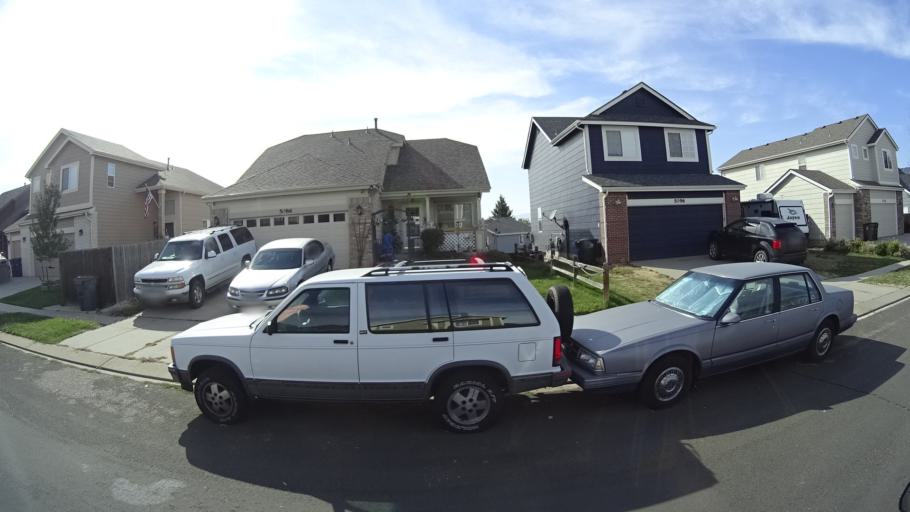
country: US
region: Colorado
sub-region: El Paso County
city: Cimarron Hills
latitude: 38.9073
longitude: -104.6920
